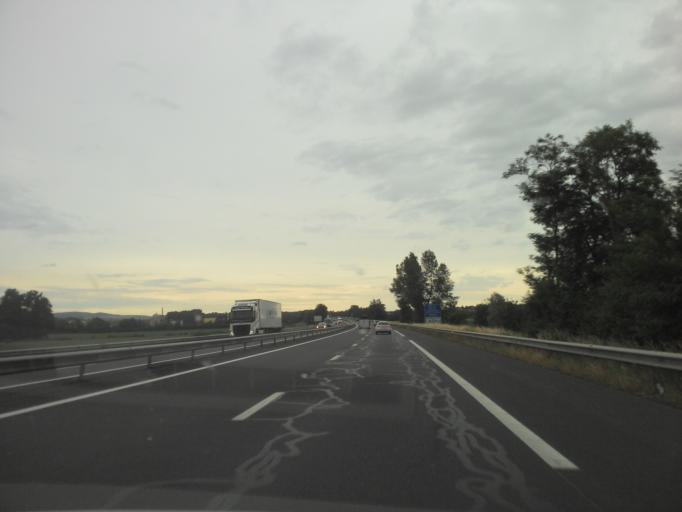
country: FR
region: Auvergne
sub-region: Departement du Puy-de-Dome
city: Riom
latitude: 45.9094
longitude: 3.1537
